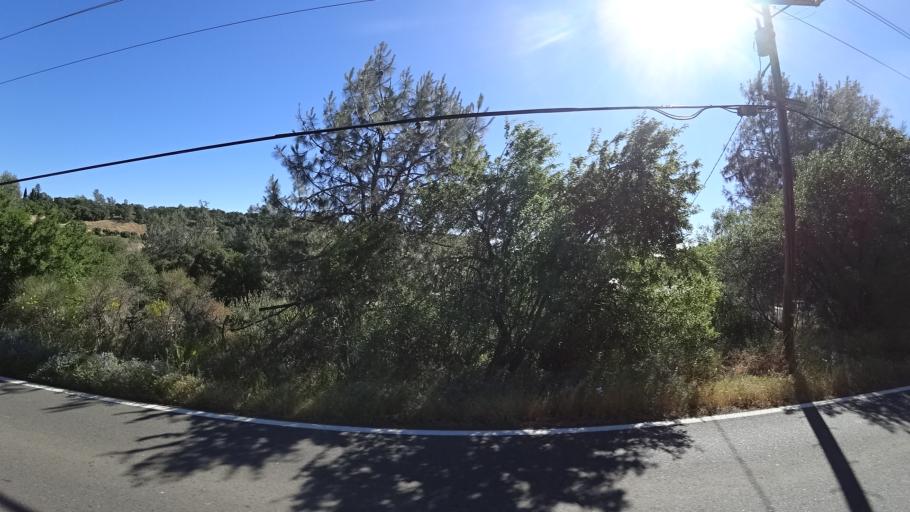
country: US
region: California
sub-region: Placer County
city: Newcastle
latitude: 38.8775
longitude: -121.1353
